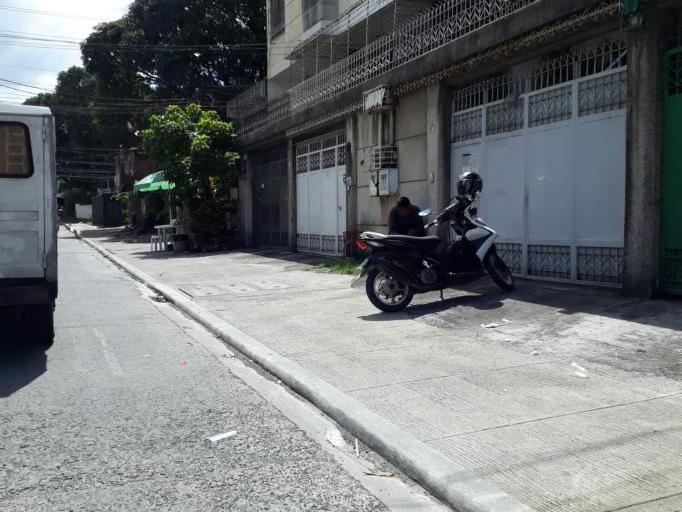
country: PH
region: Calabarzon
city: Del Monte
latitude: 14.6306
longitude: 121.0002
